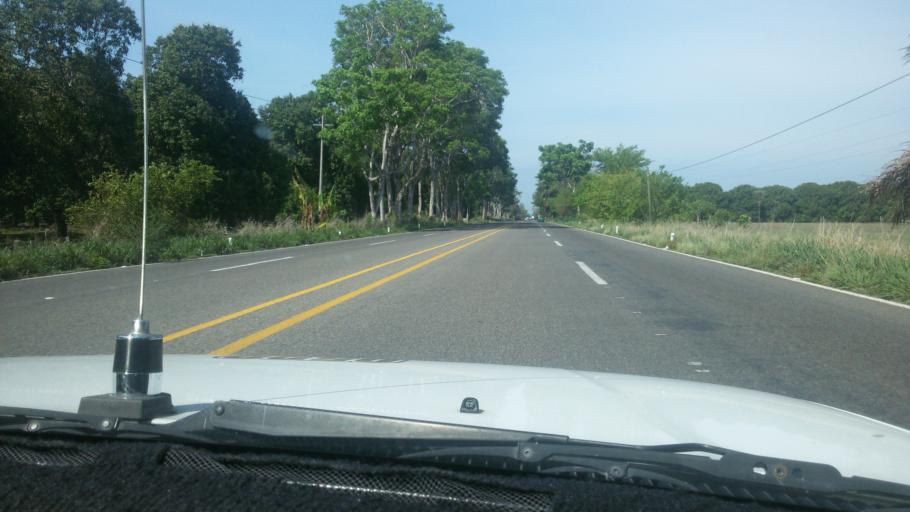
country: MX
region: Chiapas
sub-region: Tapachula
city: Congregacion Reforma
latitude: 14.8079
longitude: -92.3487
